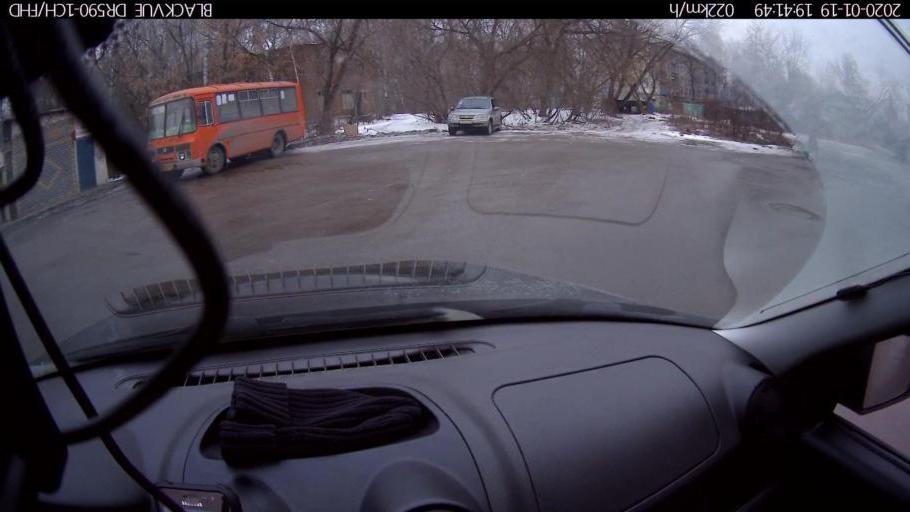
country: RU
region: Nizjnij Novgorod
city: Nizhniy Novgorod
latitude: 56.3011
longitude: 43.9119
